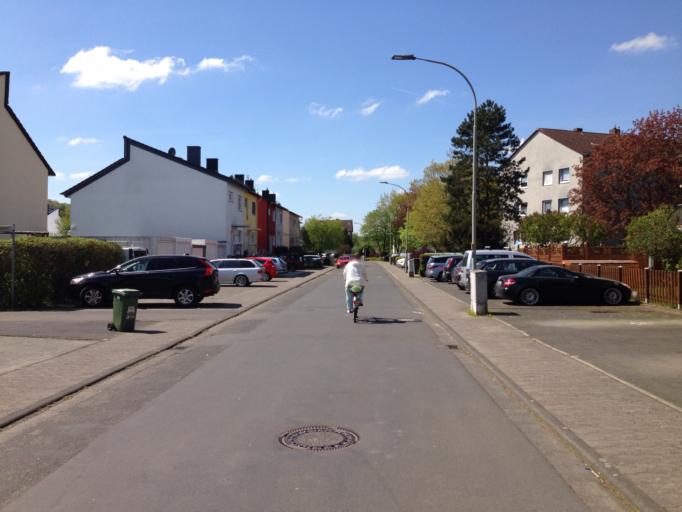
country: DE
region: Hesse
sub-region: Regierungsbezirk Giessen
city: Lich
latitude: 50.5171
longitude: 8.8099
